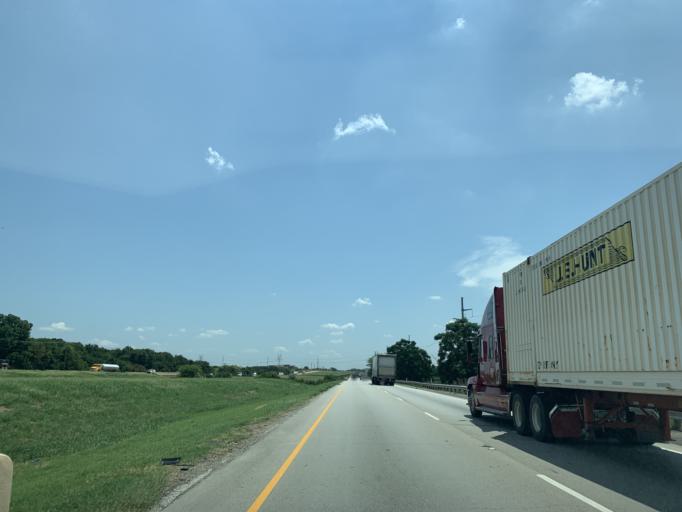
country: US
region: Texas
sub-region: Denton County
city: Roanoke
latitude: 33.0208
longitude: -97.2505
